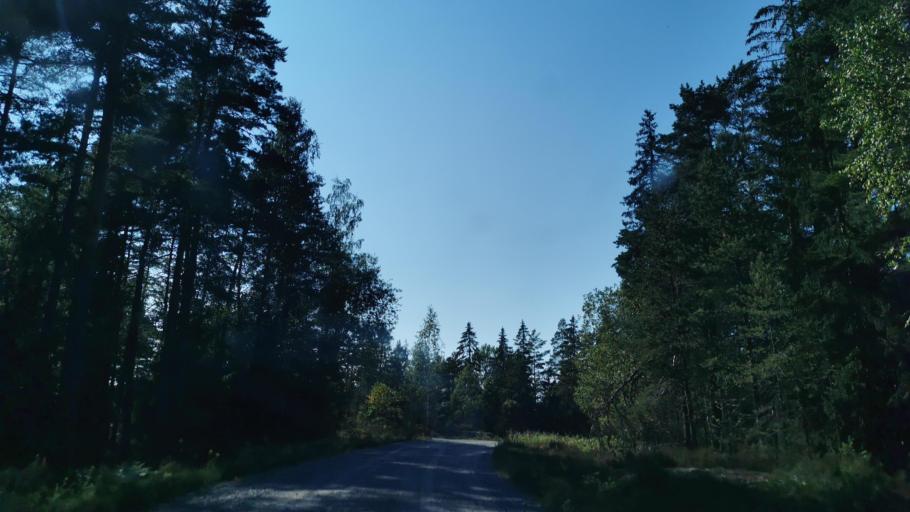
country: SE
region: OEstergoetland
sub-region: Norrkopings Kommun
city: Jursla
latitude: 58.7107
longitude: 16.1698
